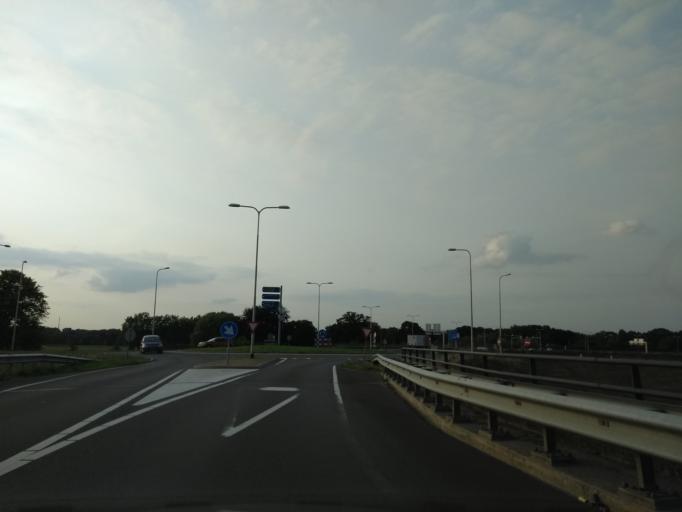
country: NL
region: Overijssel
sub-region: Gemeente Wierden
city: Wierden
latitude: 52.3513
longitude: 6.6113
